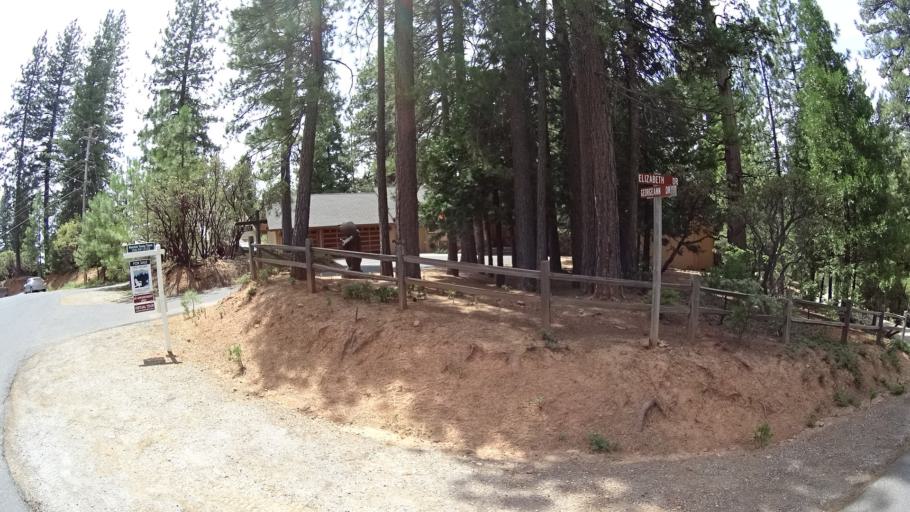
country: US
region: California
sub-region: Calaveras County
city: Arnold
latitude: 38.2435
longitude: -120.3469
